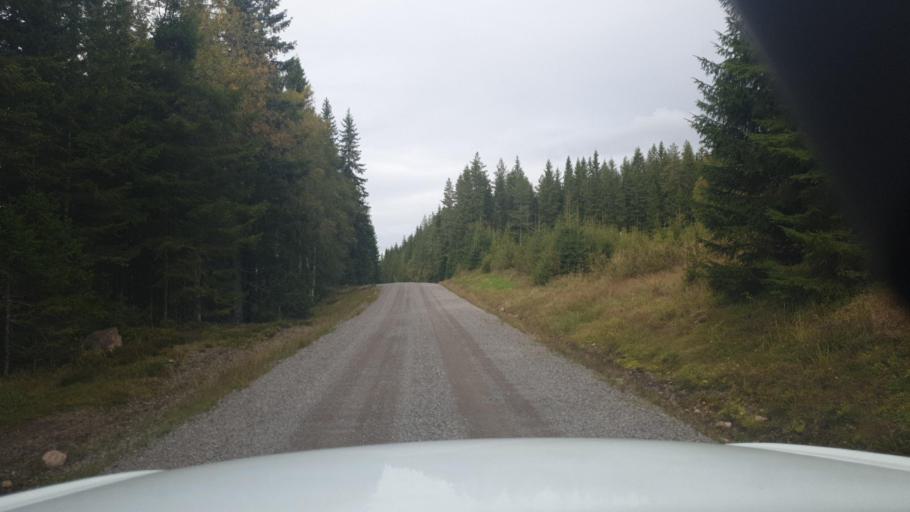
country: SE
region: Vaermland
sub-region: Eda Kommun
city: Charlottenberg
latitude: 60.0914
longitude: 12.6156
